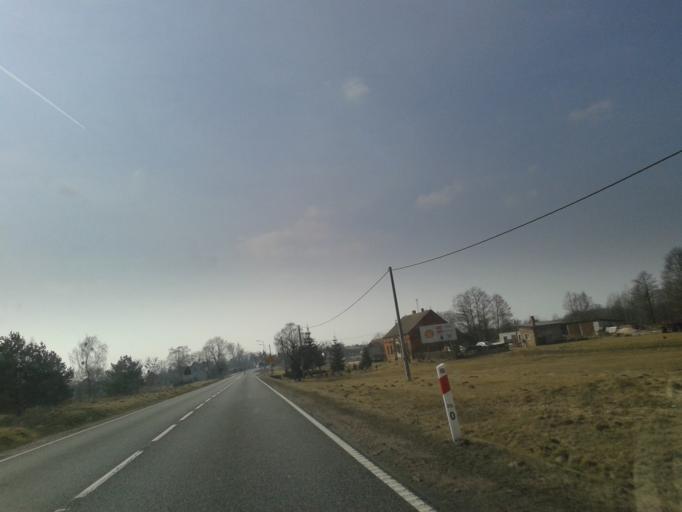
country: PL
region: Pomeranian Voivodeship
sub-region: Powiat czluchowski
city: Debrzno
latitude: 53.5742
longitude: 17.0854
